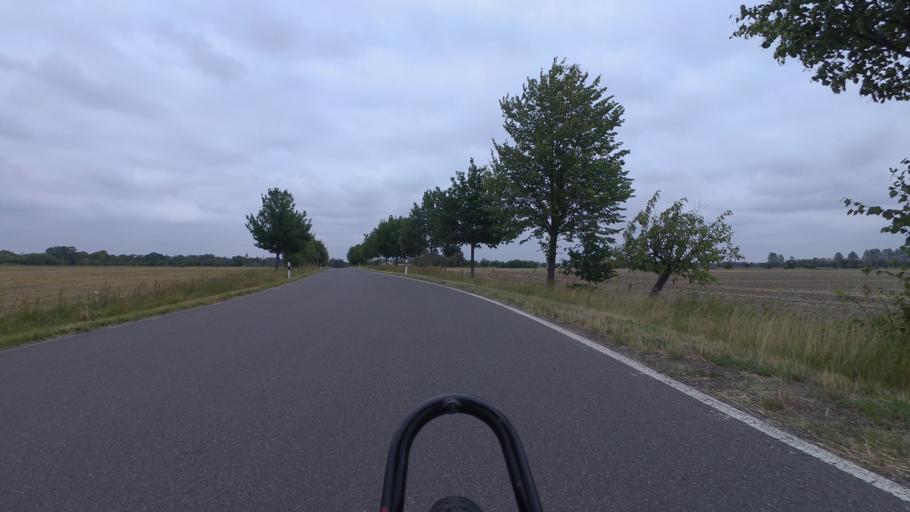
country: DE
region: Brandenburg
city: Beelitz
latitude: 52.2220
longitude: 12.9797
